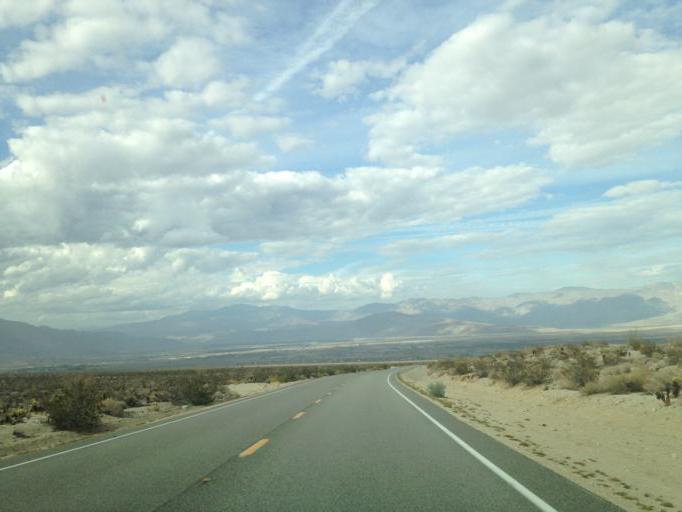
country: US
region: California
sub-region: San Diego County
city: Borrego Springs
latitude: 33.1670
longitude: -116.3358
